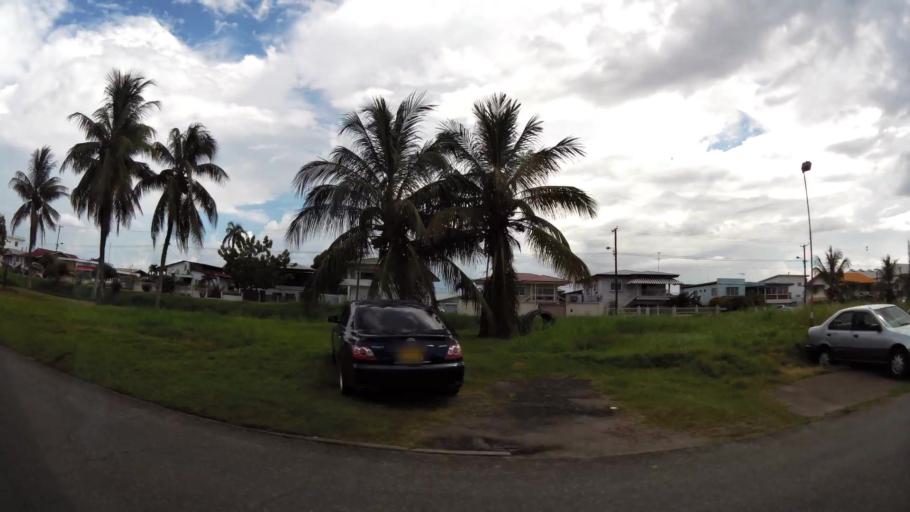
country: SR
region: Paramaribo
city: Paramaribo
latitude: 5.8401
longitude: -55.1384
